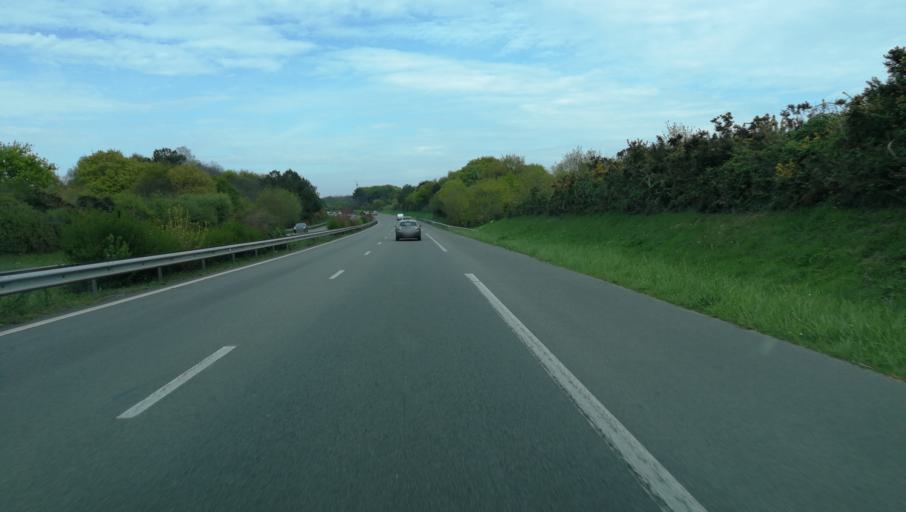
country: FR
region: Pays de la Loire
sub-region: Departement de la Loire-Atlantique
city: Saint-Andre-des-Eaux
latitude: 47.2827
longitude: -2.2821
